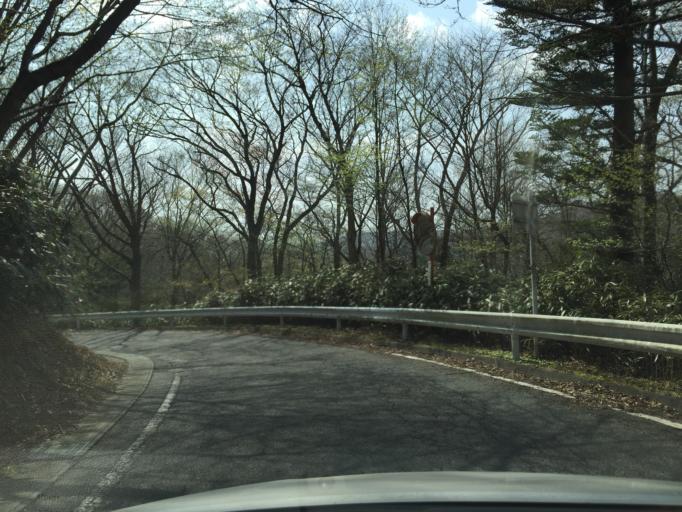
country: JP
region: Fukushima
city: Iwaki
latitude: 37.2024
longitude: 140.8519
